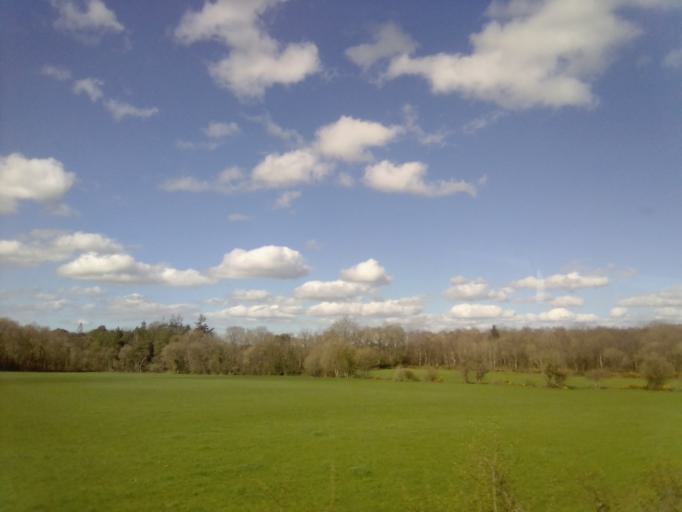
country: IE
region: Munster
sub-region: County Cork
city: Kanturk
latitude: 52.1286
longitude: -8.8544
